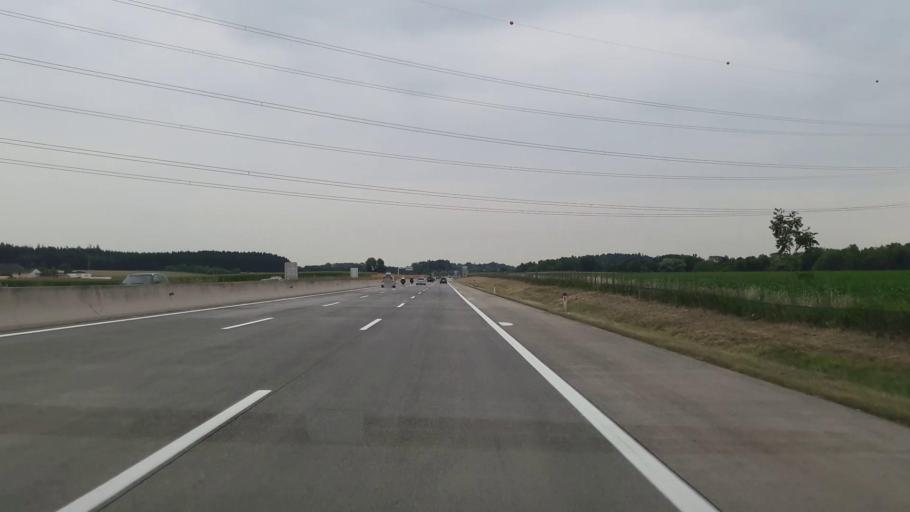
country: AT
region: Upper Austria
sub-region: Wels-Land
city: Sattledt
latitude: 48.0853
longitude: 14.0635
